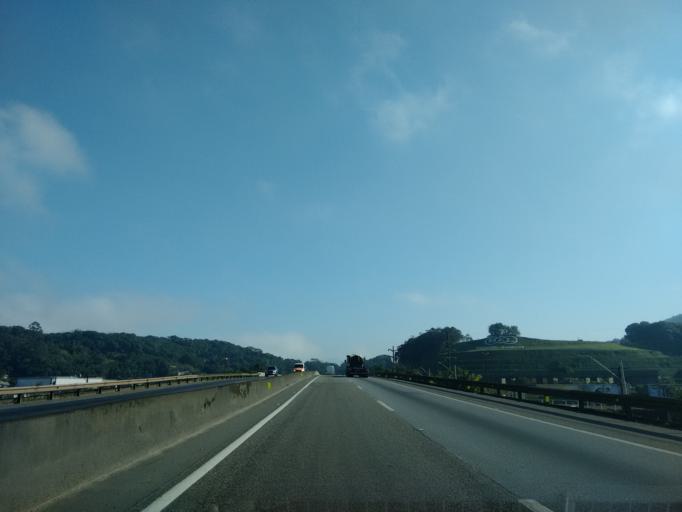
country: BR
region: Santa Catarina
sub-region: Joinville
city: Joinville
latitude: -26.3195
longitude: -48.8711
